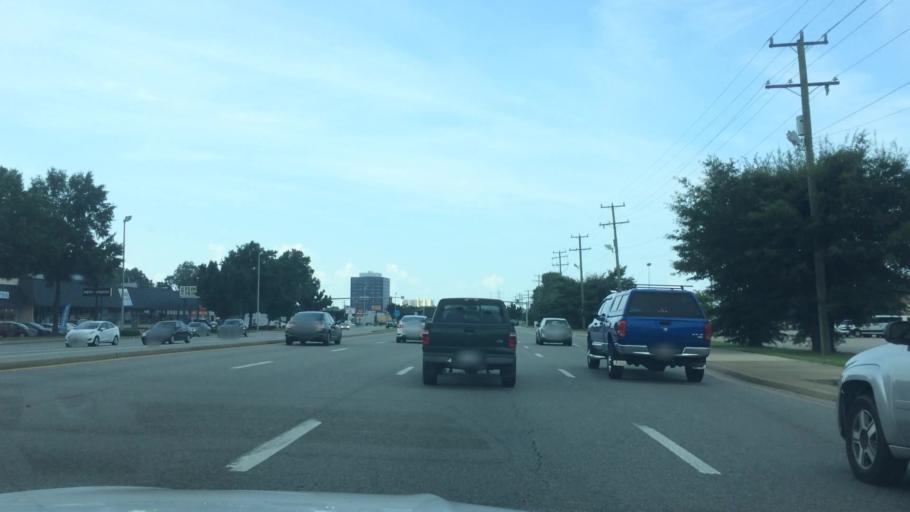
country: US
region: Virginia
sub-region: City of Newport News
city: Newport News
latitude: 37.0238
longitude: -76.4358
